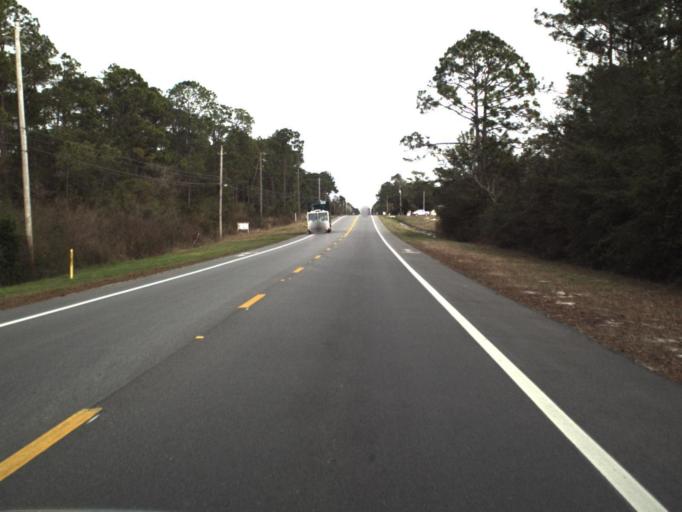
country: US
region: Florida
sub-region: Bay County
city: Callaway
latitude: 30.1528
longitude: -85.5566
